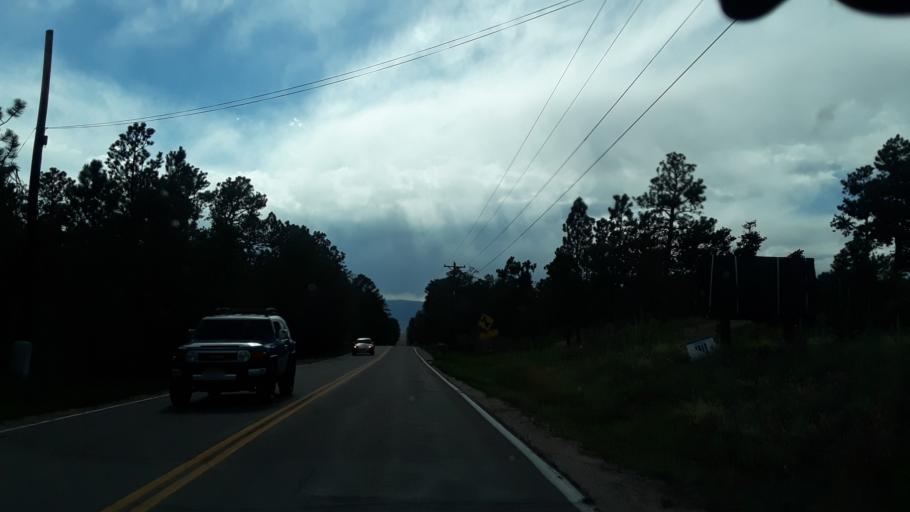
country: US
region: Colorado
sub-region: El Paso County
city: Black Forest
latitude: 39.0131
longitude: -104.7232
